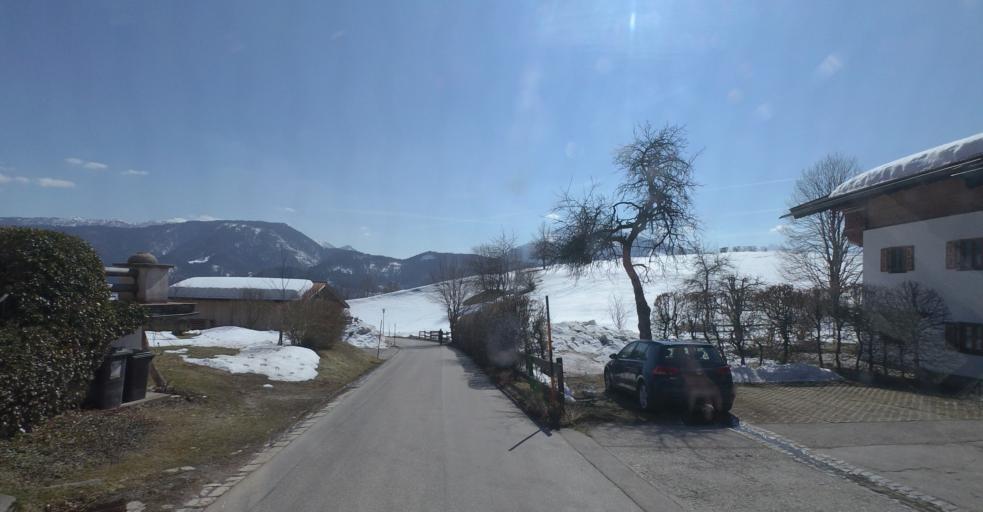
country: DE
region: Bavaria
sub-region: Upper Bavaria
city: Reit im Winkl
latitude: 47.6786
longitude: 12.4492
